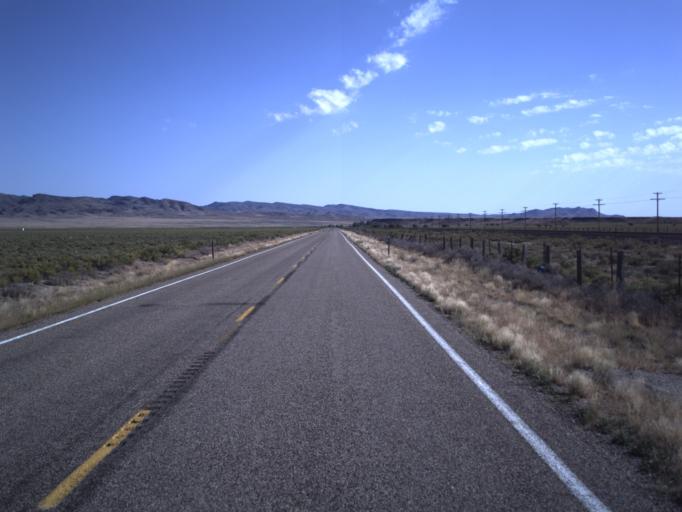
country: US
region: Utah
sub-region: Beaver County
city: Milford
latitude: 38.6946
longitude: -112.9742
